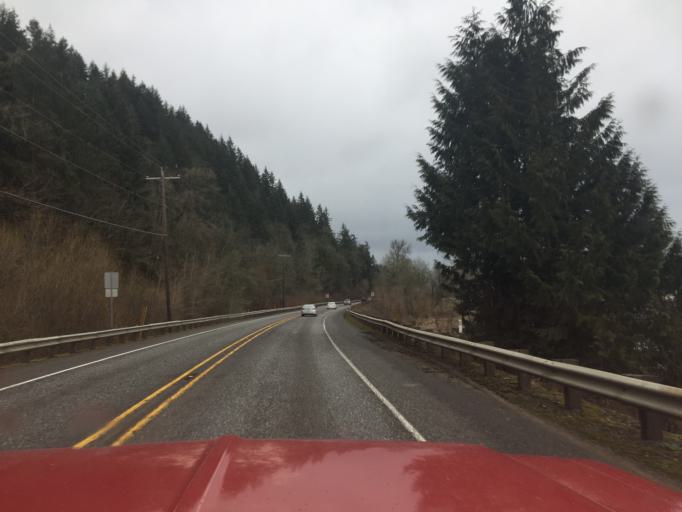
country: US
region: Oregon
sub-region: Columbia County
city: Rainier
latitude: 46.0503
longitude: -122.8982
